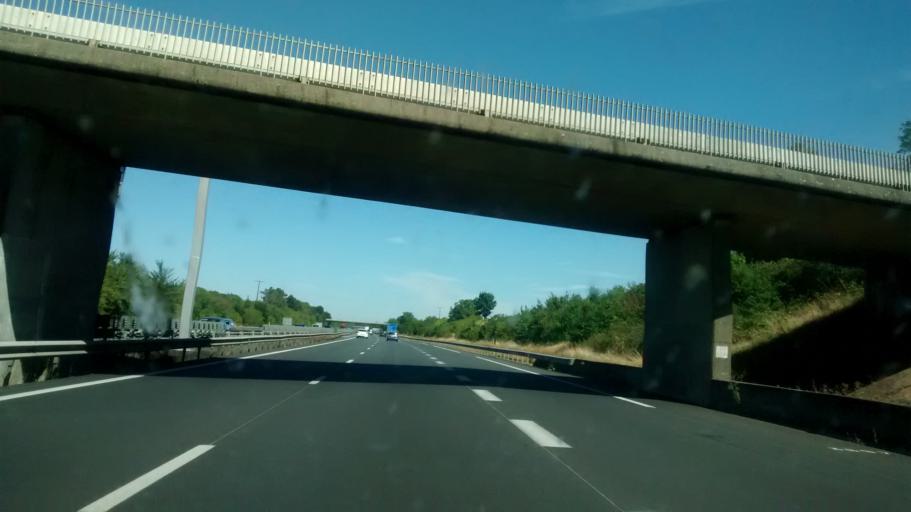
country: FR
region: Poitou-Charentes
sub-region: Departement des Deux-Sevres
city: Vouille
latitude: 46.3078
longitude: -0.3561
